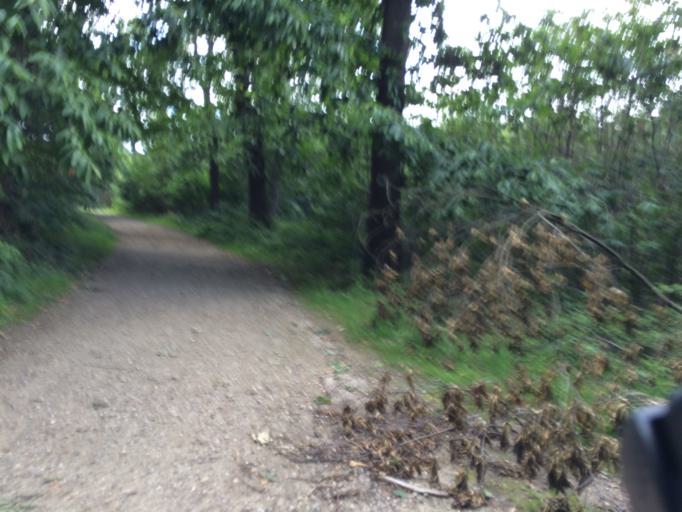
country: FR
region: Ile-de-France
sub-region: Departement de l'Essonne
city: Verrieres-le-Buisson
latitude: 48.7543
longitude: 2.2611
